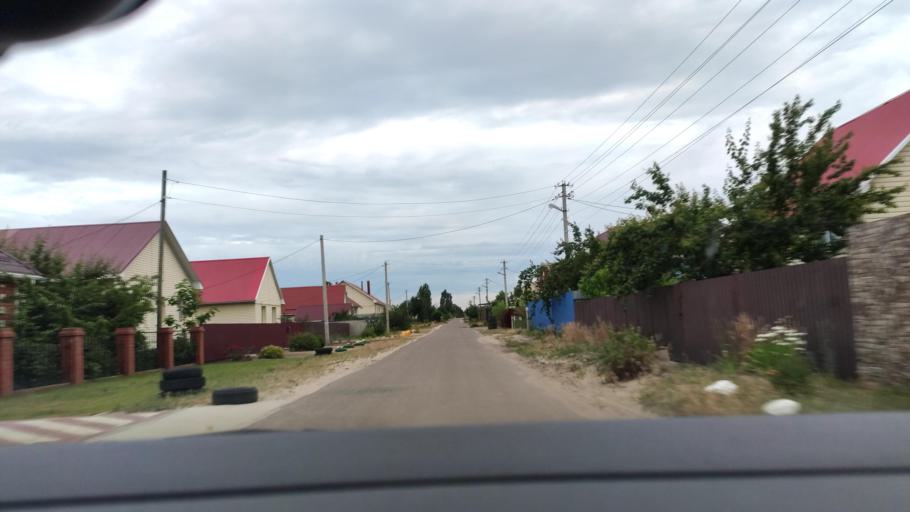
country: RU
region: Voronezj
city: Maslovka
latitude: 51.5707
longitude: 39.2505
